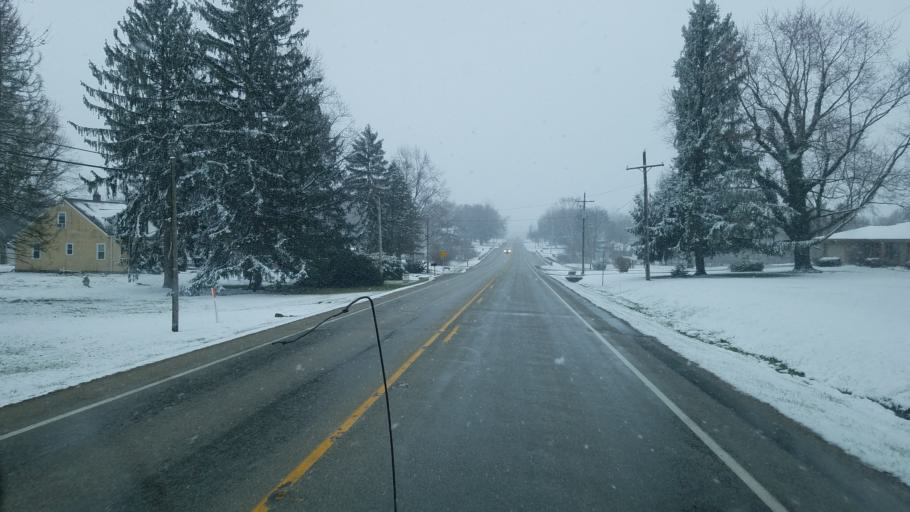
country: US
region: Indiana
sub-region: Wayne County
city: Richmond
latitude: 39.8925
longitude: -84.9441
